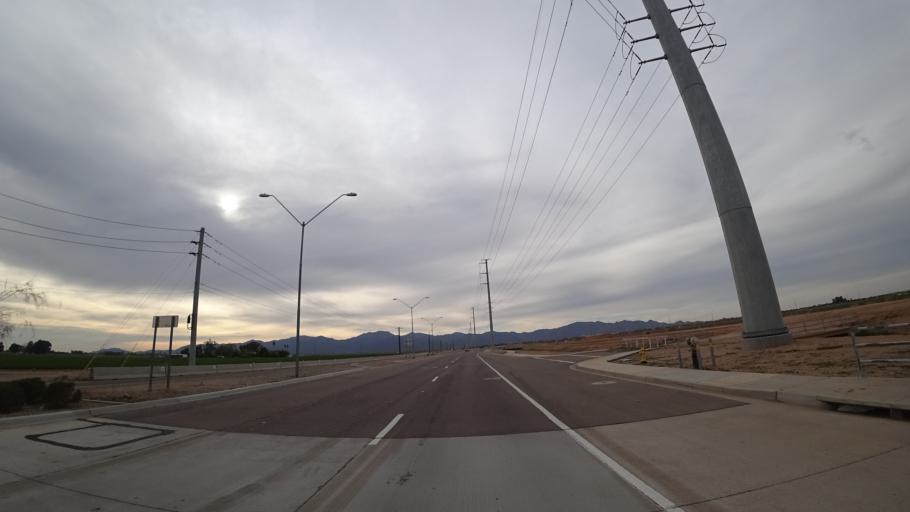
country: US
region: Arizona
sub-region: Maricopa County
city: Citrus Park
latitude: 33.5954
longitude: -112.4197
